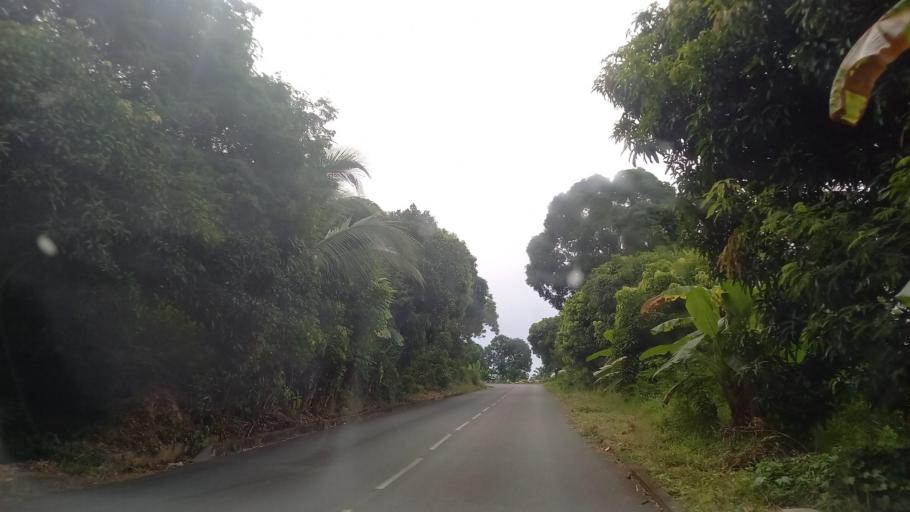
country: YT
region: Boueni
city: Boueni
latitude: -12.9016
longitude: 45.0914
